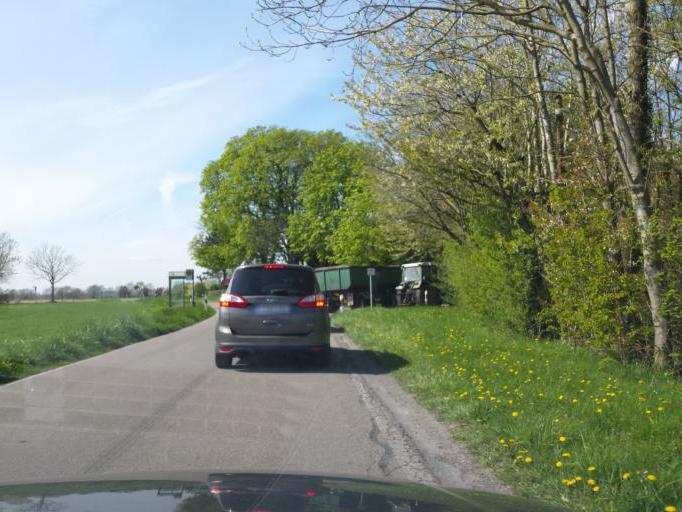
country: DE
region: North Rhine-Westphalia
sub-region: Regierungsbezirk Munster
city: Nottuln
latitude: 51.9061
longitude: 7.3775
